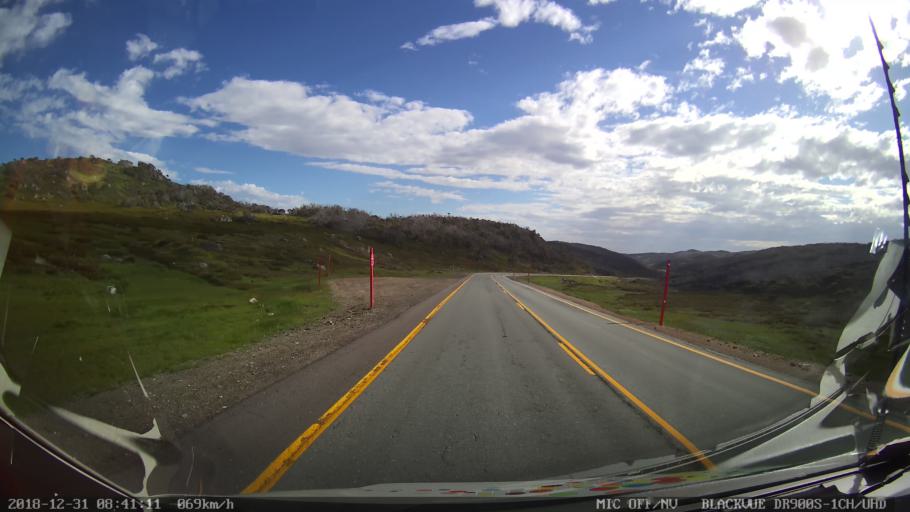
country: AU
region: New South Wales
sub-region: Snowy River
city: Jindabyne
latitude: -36.3996
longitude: 148.4200
